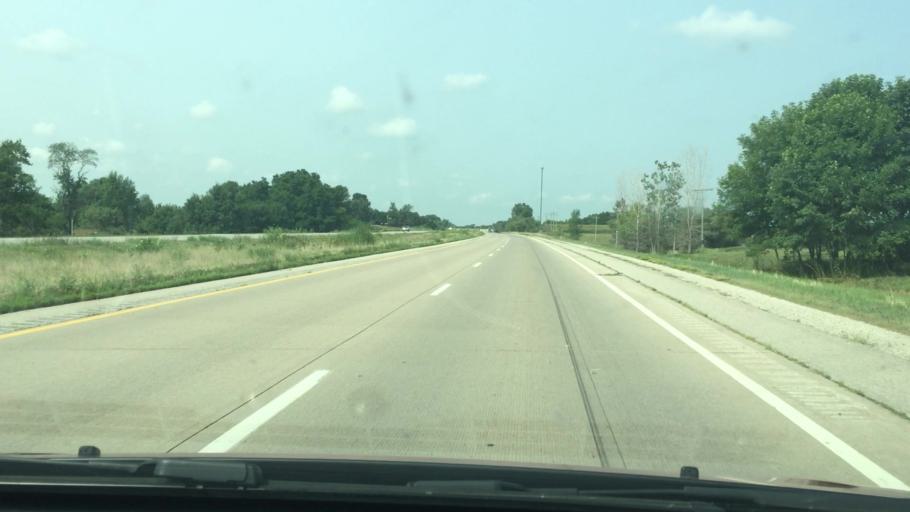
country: US
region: Iowa
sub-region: Cedar County
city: Durant
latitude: 41.5194
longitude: -90.8840
